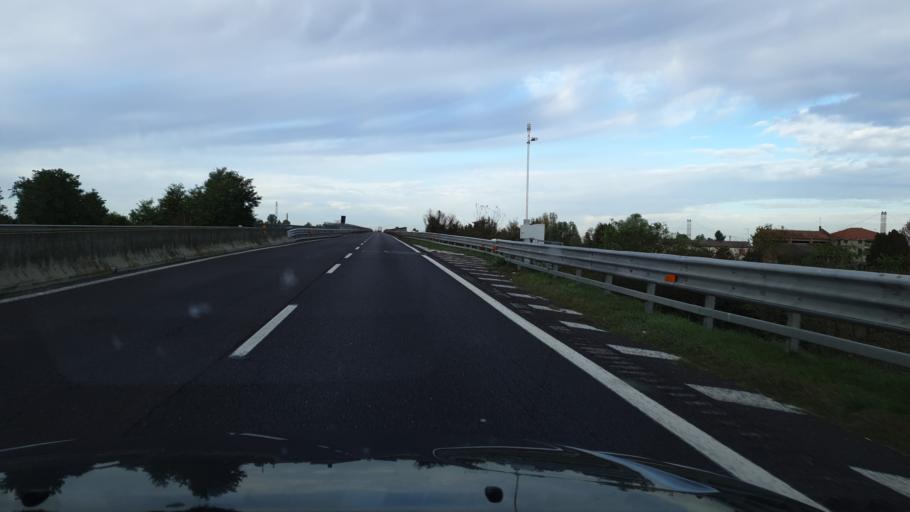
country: IT
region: Veneto
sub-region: Provincia di Padova
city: Boara Pisani
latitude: 45.0907
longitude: 11.7480
